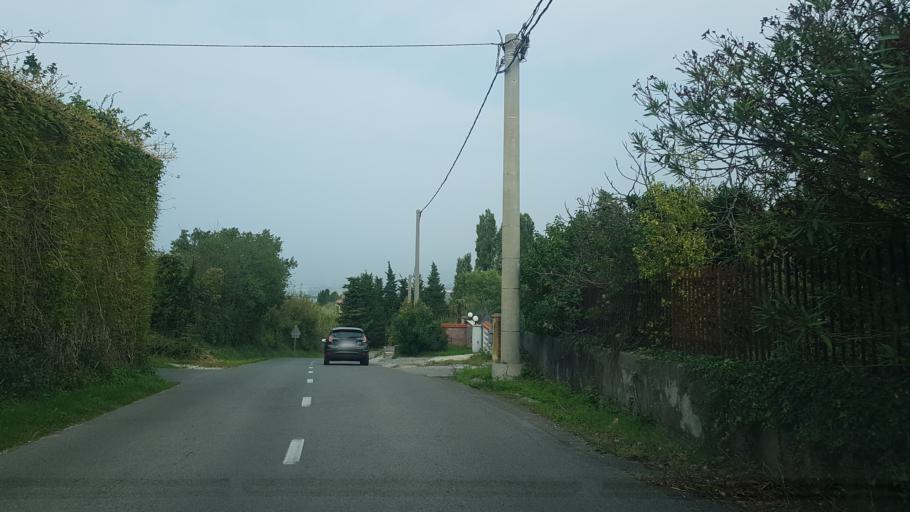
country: SI
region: Koper-Capodistria
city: Spodnje Skofije
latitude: 45.5803
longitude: 13.8035
